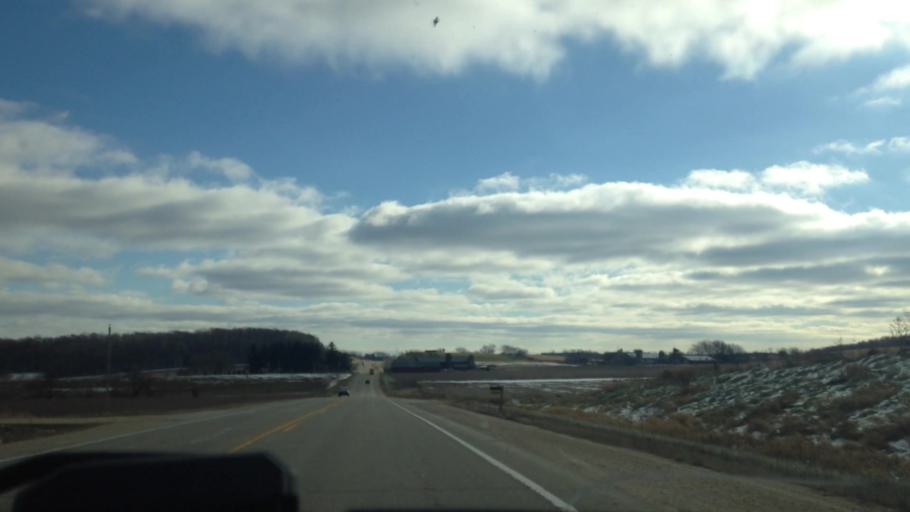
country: US
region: Wisconsin
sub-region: Dodge County
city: Theresa
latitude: 43.4364
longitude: -88.4686
